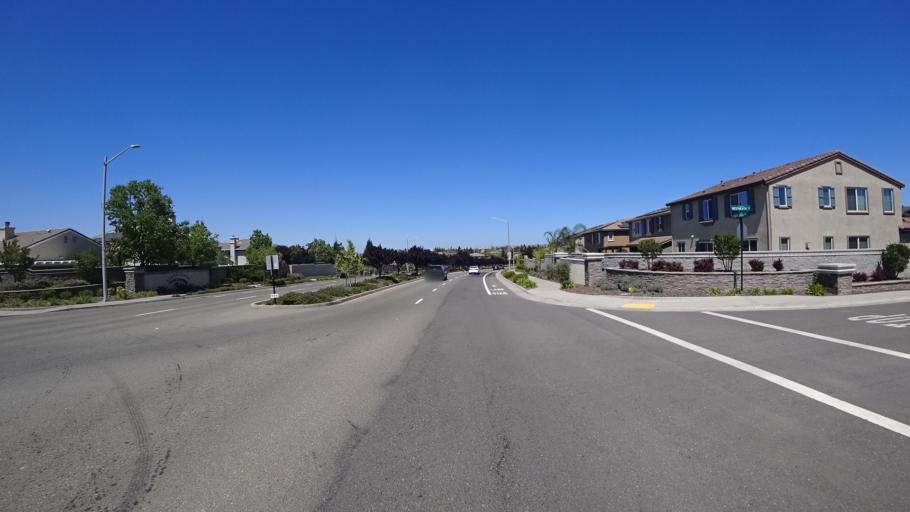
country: US
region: California
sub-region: Placer County
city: Rocklin
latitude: 38.8027
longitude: -121.2840
